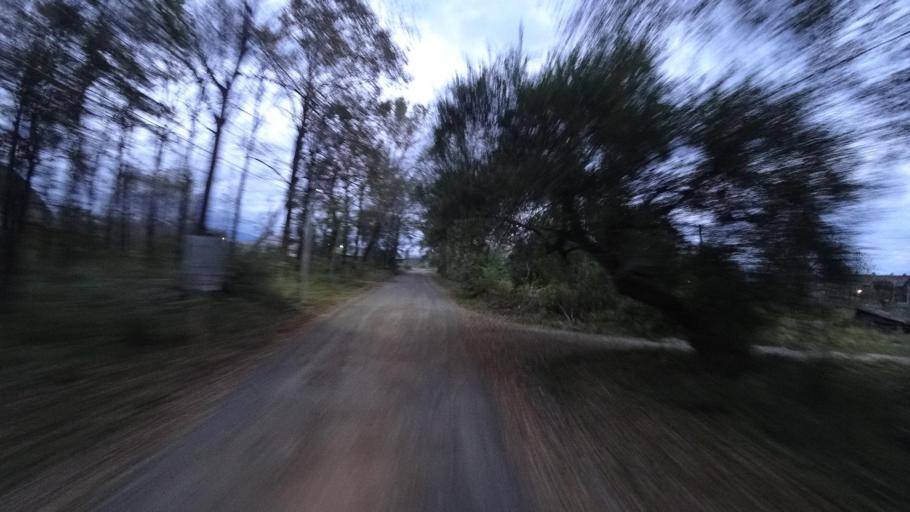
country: RU
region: Jewish Autonomous Oblast
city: Izvestkovyy
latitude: 48.9853
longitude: 131.5461
